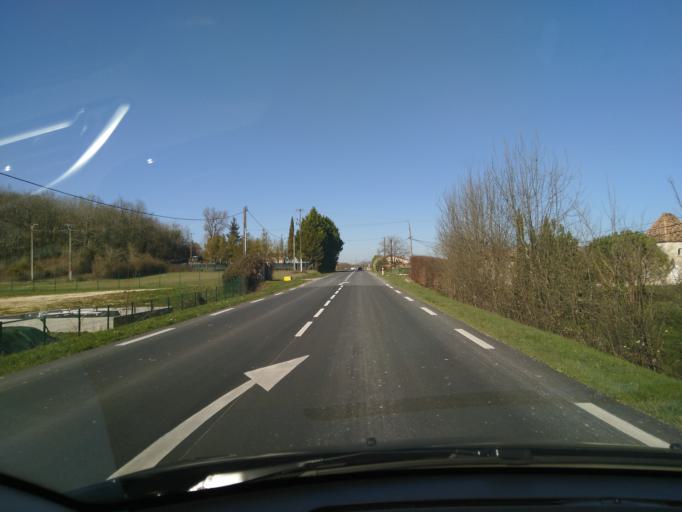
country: FR
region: Aquitaine
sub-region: Departement de la Dordogne
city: Monbazillac
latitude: 44.7470
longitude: 0.5370
